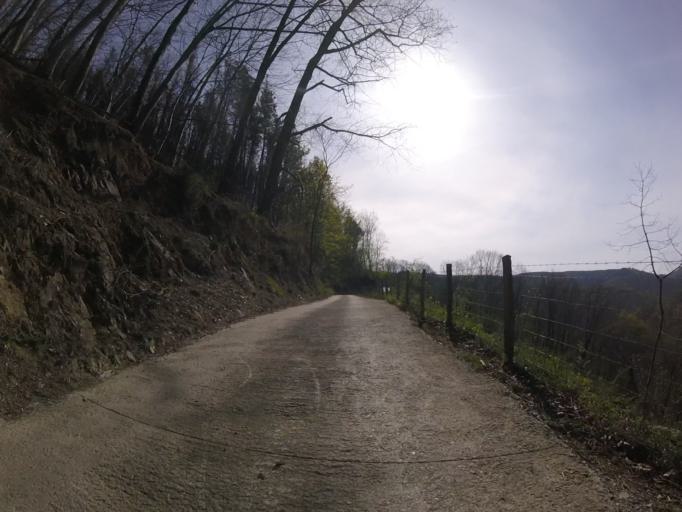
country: ES
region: Basque Country
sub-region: Provincia de Guipuzcoa
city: Errenteria
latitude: 43.2770
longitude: -1.8418
